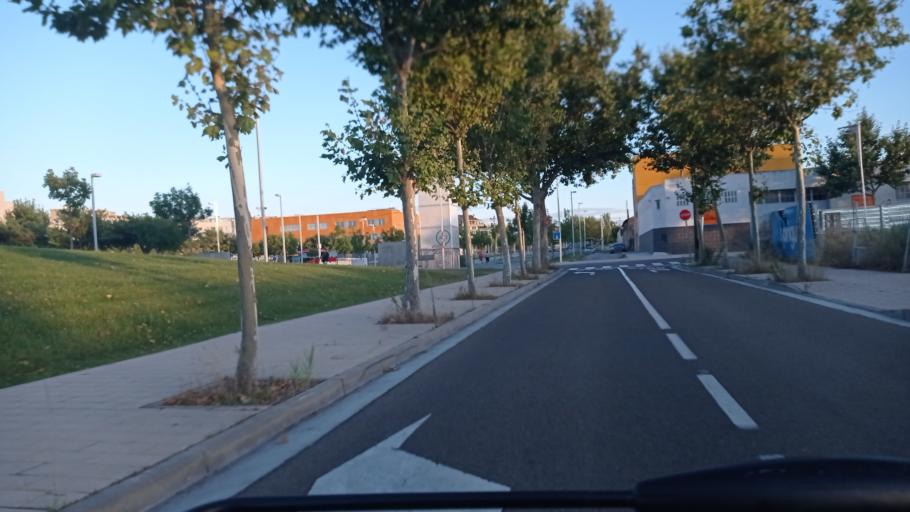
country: ES
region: Aragon
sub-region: Provincia de Zaragoza
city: Oliver-Valdefierro, Oliver, Valdefierro
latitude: 41.6591
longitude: -0.9252
